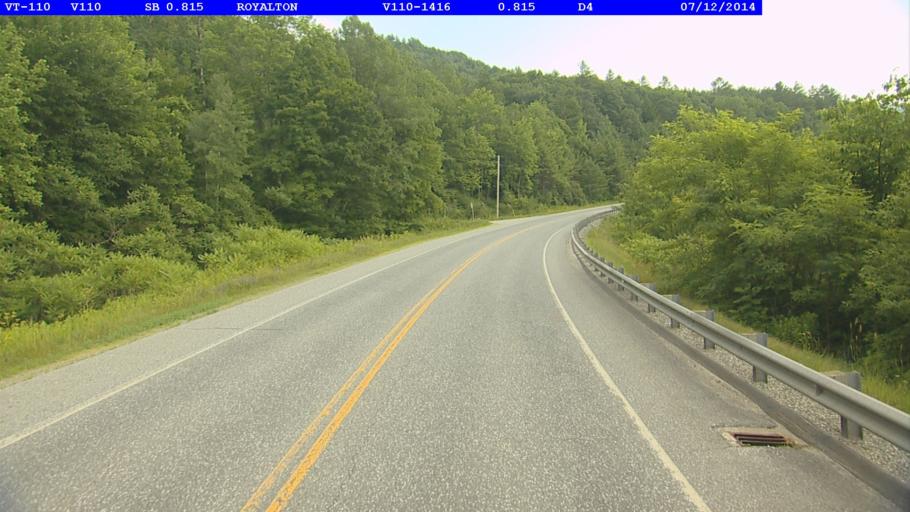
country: US
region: Vermont
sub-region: Orange County
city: Chelsea
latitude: 43.8338
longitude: -72.5117
